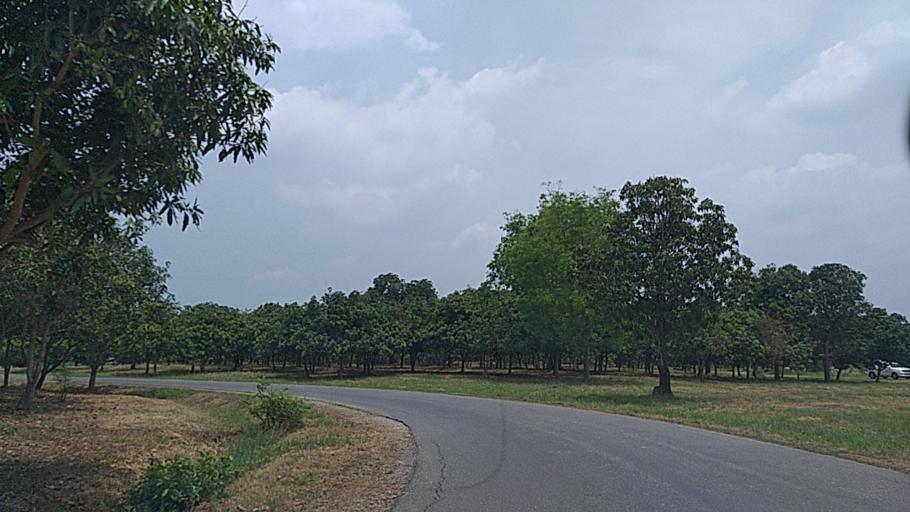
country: TH
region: Bangkok
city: Thawi Watthana
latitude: 13.7716
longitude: 100.3115
